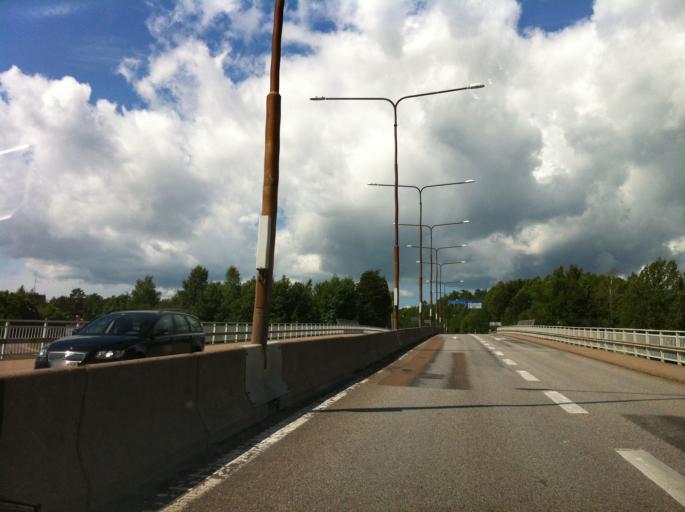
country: SE
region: Vaermland
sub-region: Saffle Kommun
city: Saeffle
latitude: 59.1357
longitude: 12.9192
